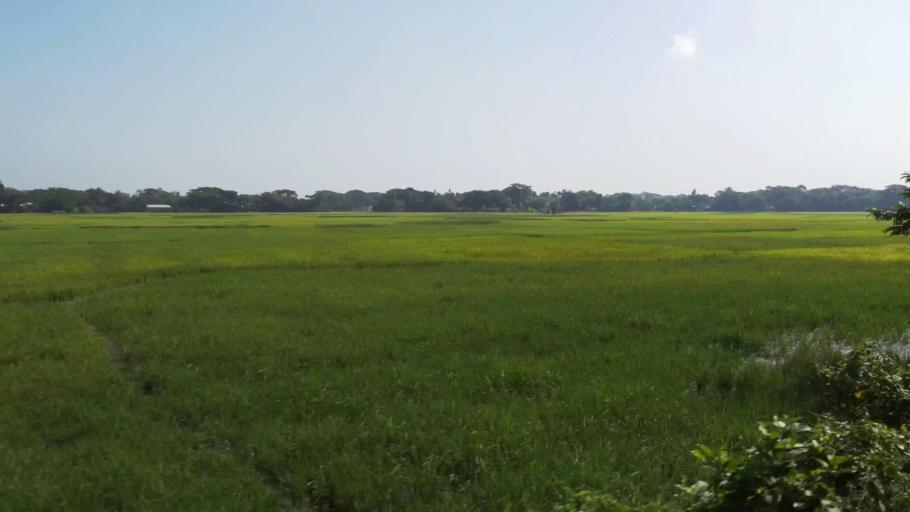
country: BD
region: Dhaka
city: Gafargaon
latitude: 24.5188
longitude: 90.5100
